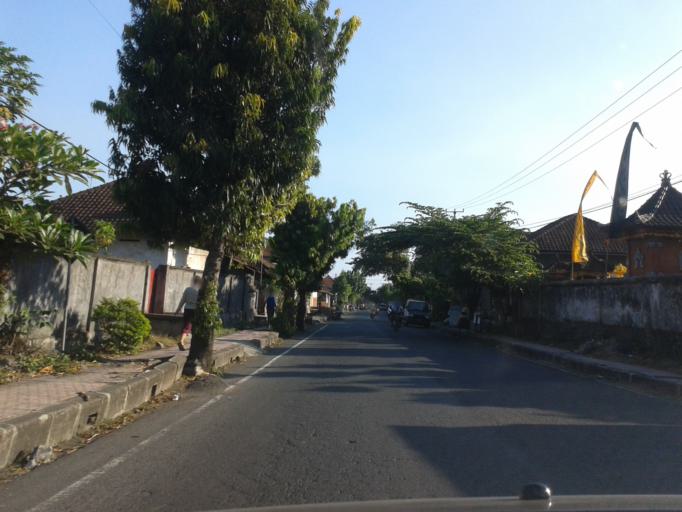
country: ID
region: Bali
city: Klungkung
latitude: -8.5151
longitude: 115.4014
